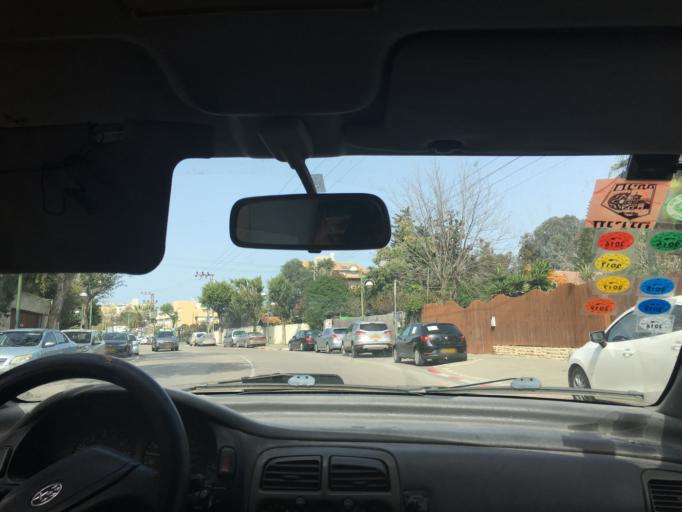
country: IL
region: Tel Aviv
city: Ramat HaSharon
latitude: 32.1354
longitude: 34.8455
